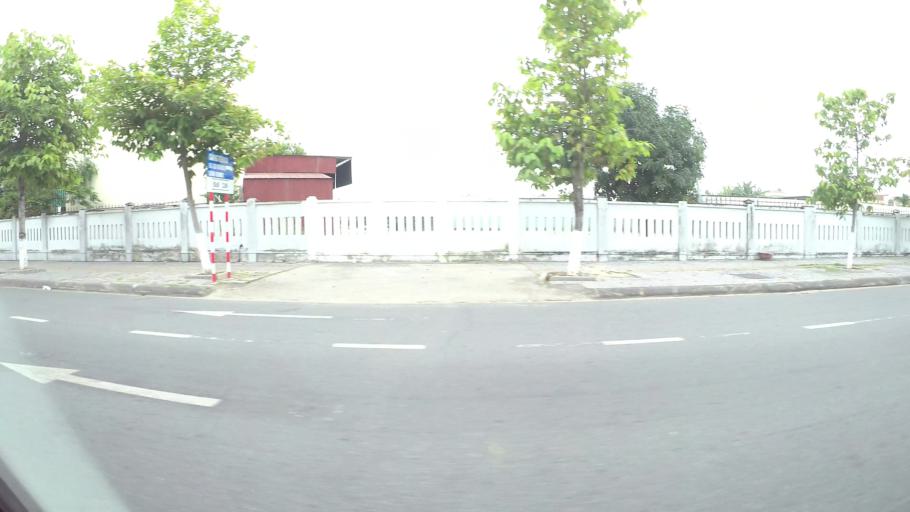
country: VN
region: Da Nang
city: Da Nang
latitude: 16.0509
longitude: 108.2078
